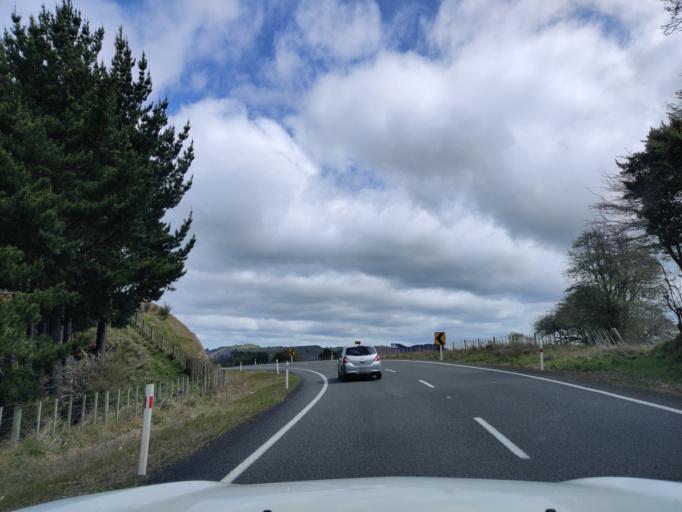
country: NZ
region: Manawatu-Wanganui
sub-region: Wanganui District
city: Wanganui
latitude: -39.7890
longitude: 175.2159
